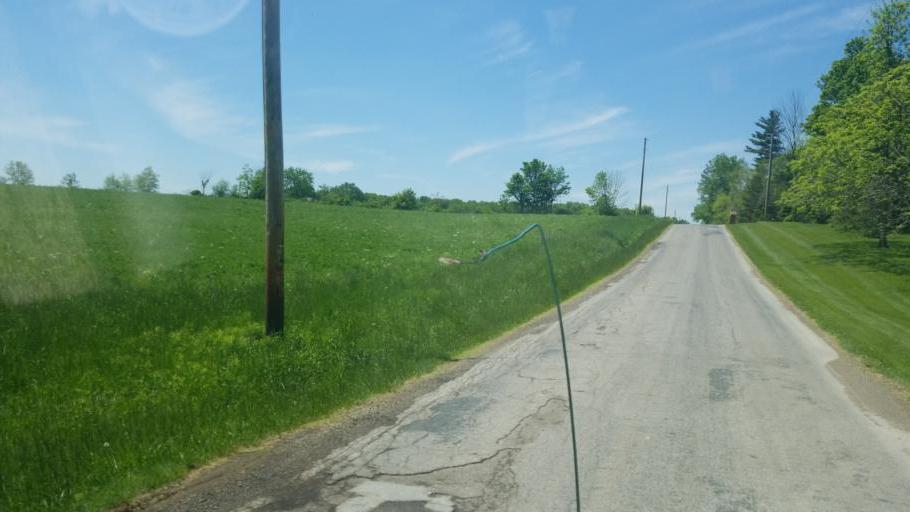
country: US
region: Ohio
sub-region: Huron County
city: Greenwich
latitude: 40.9680
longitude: -82.4253
